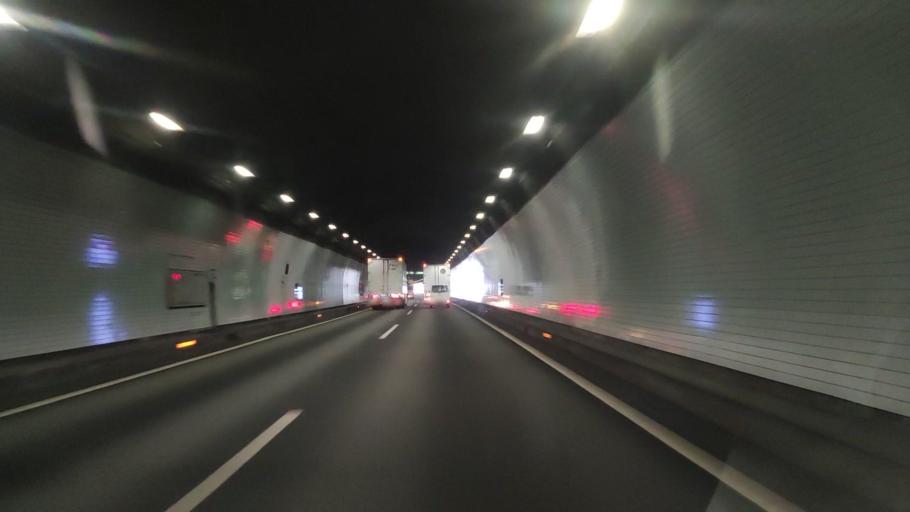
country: JP
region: Tokyo
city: Fussa
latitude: 35.7475
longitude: 139.2819
